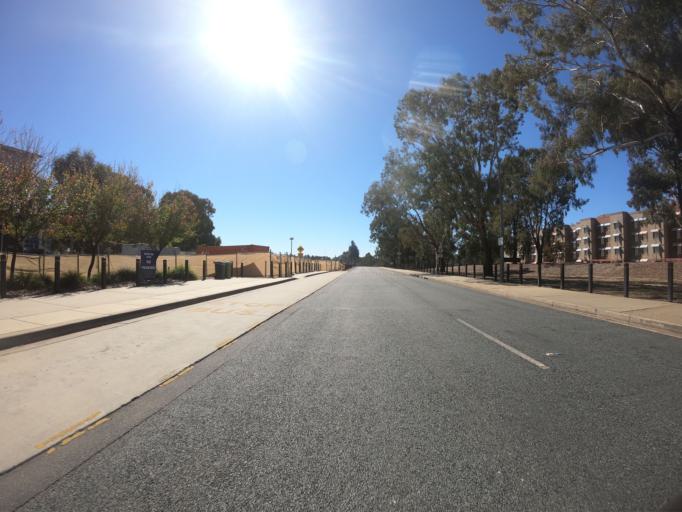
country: AU
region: Australian Capital Territory
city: Kaleen
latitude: -35.2446
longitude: 149.1025
